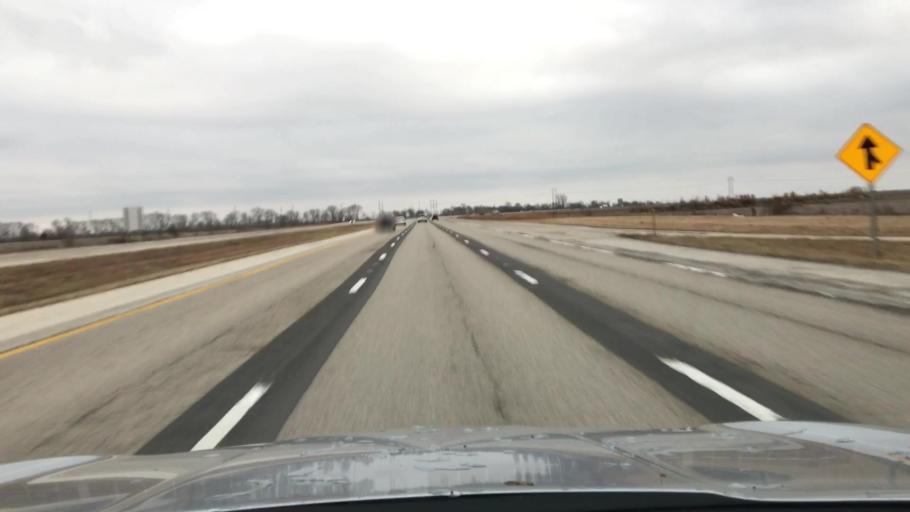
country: US
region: Illinois
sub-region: Logan County
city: Lincoln
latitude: 40.1082
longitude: -89.4166
